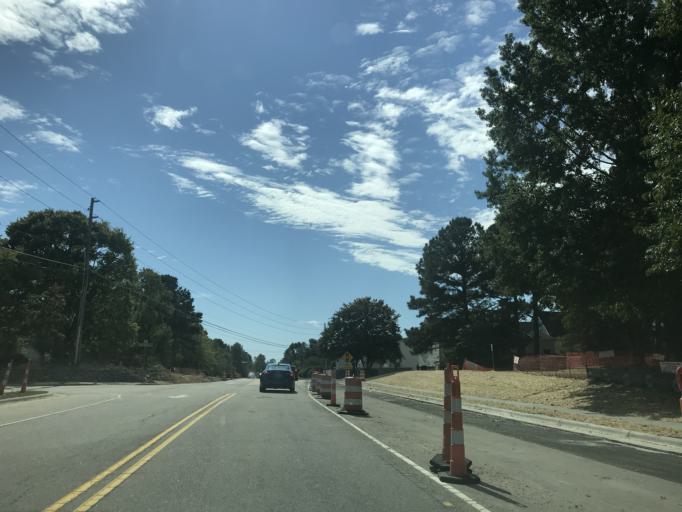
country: US
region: North Carolina
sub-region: Wake County
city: Knightdale
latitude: 35.8585
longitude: -78.5667
